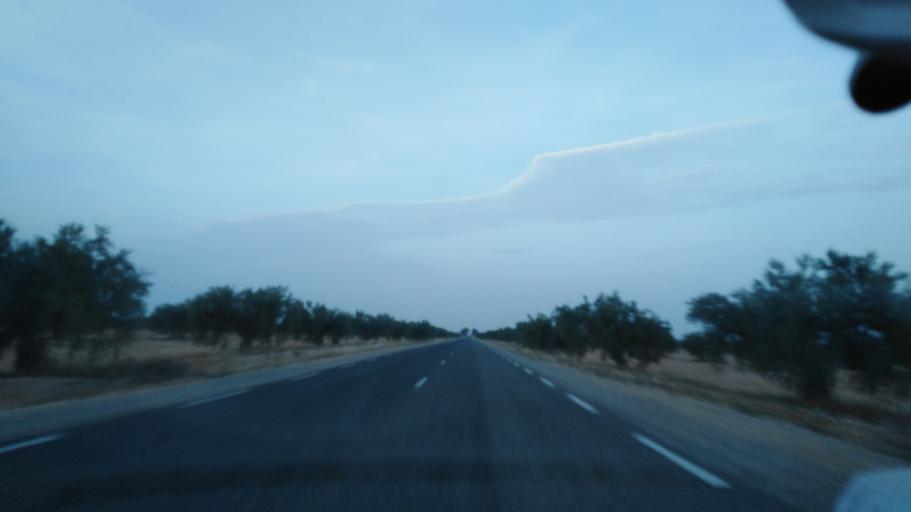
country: TN
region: Al Mahdiyah
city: Shurban
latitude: 34.9382
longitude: 10.3955
